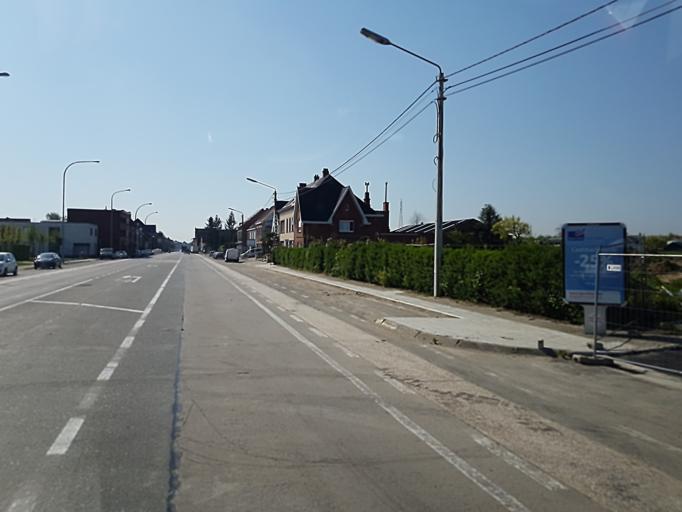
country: BE
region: Flanders
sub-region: Provincie West-Vlaanderen
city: Menen
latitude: 50.8132
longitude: 3.1209
